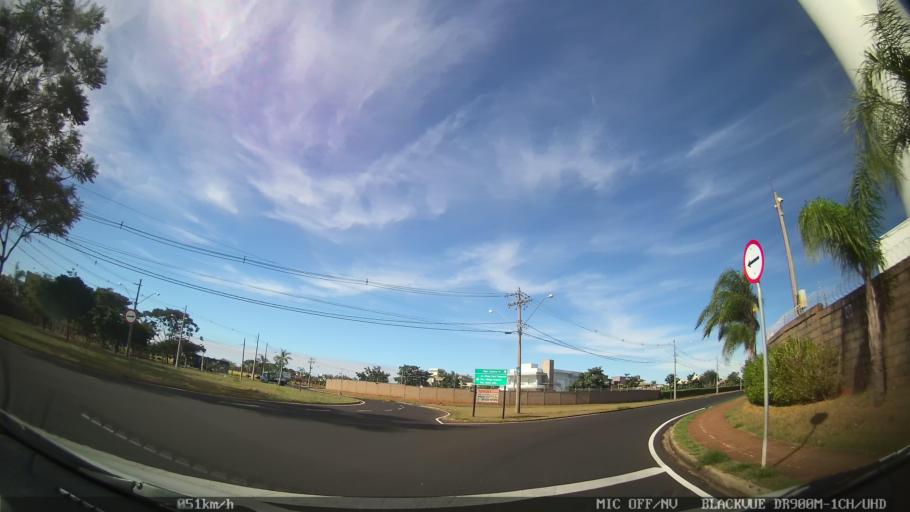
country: BR
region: Sao Paulo
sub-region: Sao Jose Do Rio Preto
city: Sao Jose do Rio Preto
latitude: -20.8069
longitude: -49.3320
